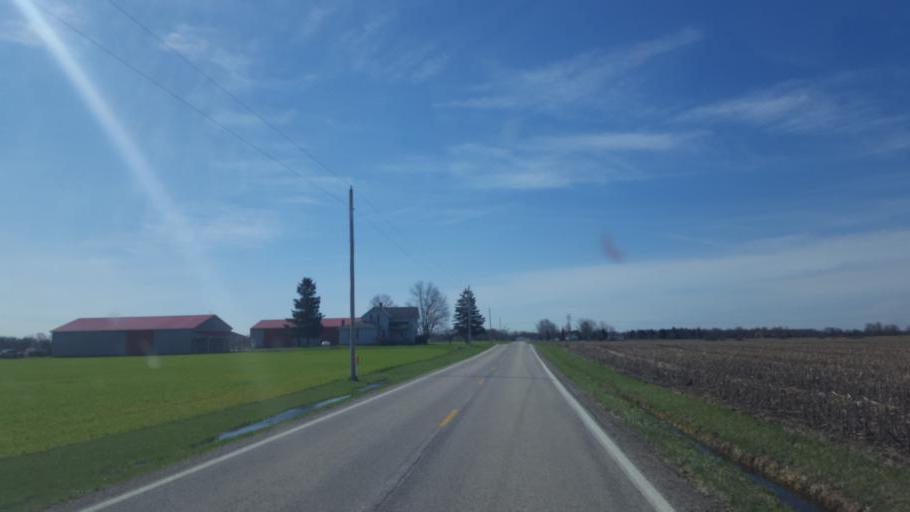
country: US
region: Ohio
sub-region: Morrow County
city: Cardington
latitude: 40.4950
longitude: -82.9632
